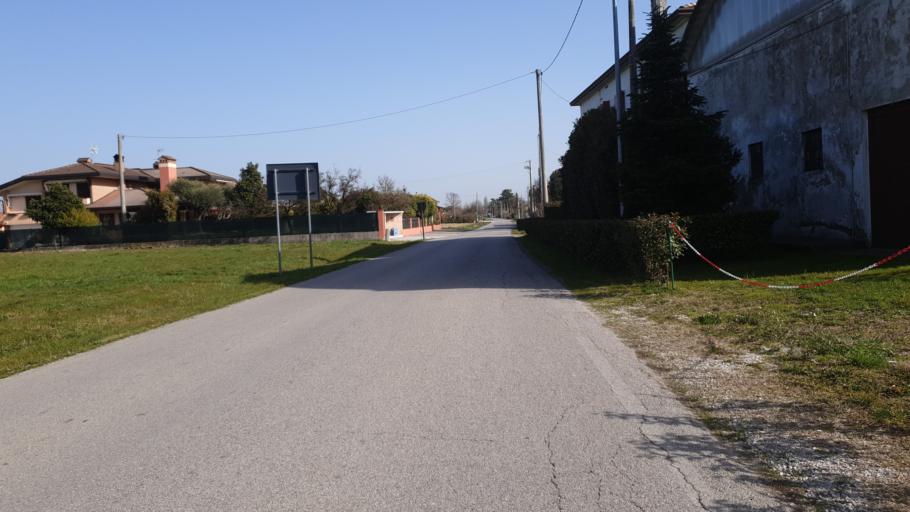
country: IT
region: Veneto
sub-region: Provincia di Padova
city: Cavino
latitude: 45.5221
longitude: 11.8685
